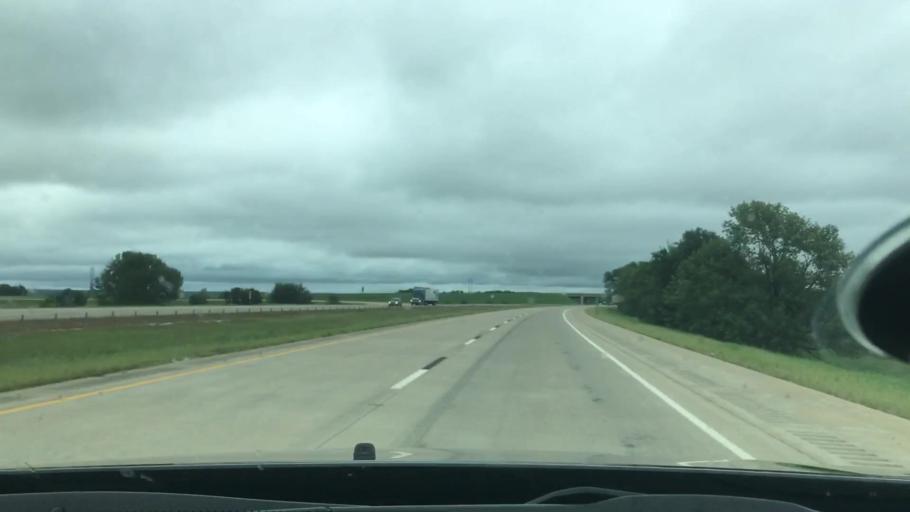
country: US
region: Oklahoma
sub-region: Muskogee County
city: Warner
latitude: 35.4878
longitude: -95.1761
